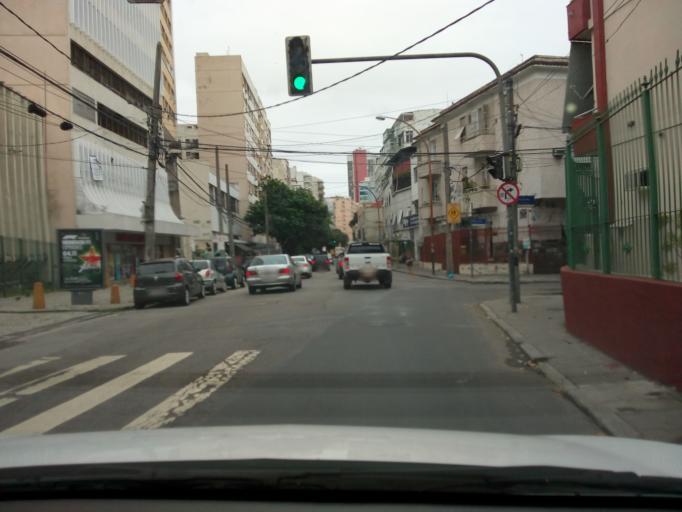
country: BR
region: Rio de Janeiro
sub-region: Rio De Janeiro
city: Rio de Janeiro
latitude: -22.9333
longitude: -43.1812
